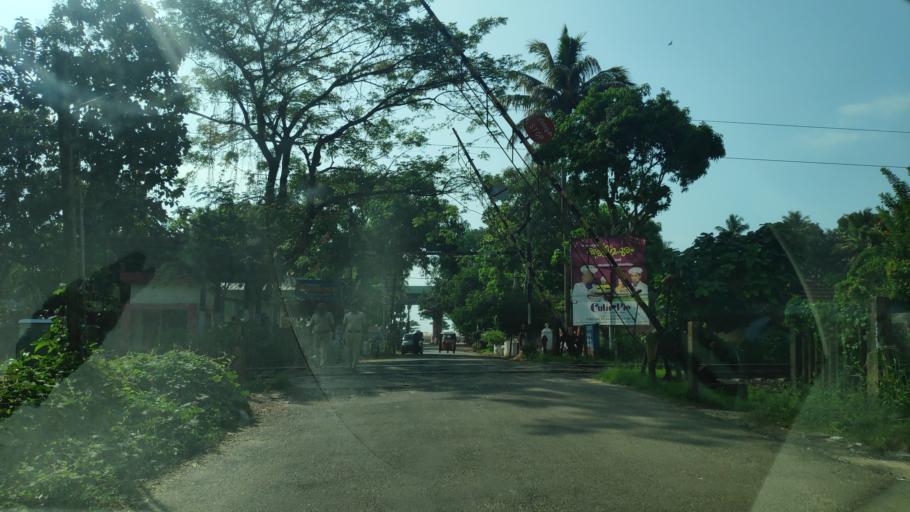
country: IN
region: Kerala
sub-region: Alappuzha
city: Alleppey
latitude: 9.4973
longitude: 76.3190
